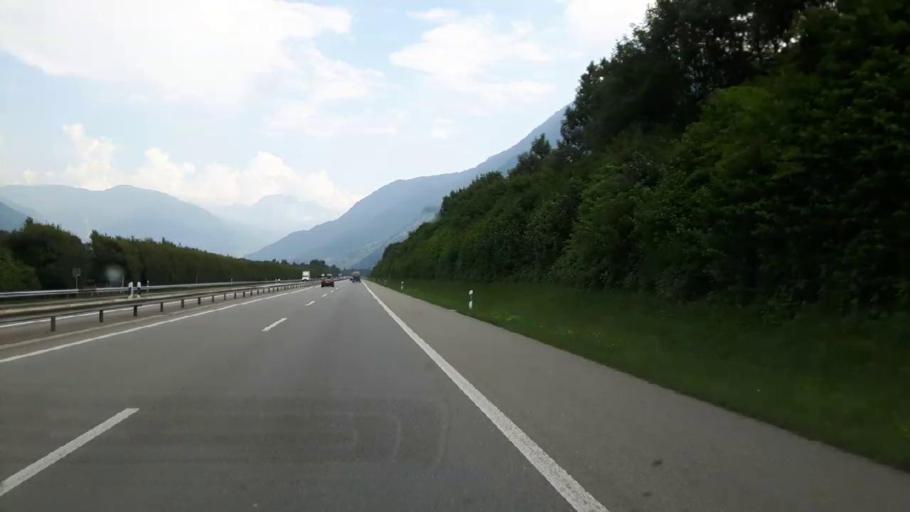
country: CH
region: Ticino
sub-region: Riviera District
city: Lodrino
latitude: 46.2946
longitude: 8.9897
